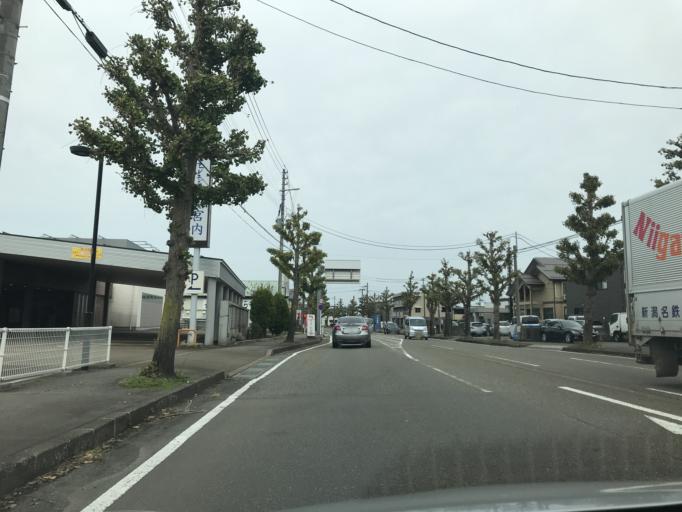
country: JP
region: Niigata
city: Nagaoka
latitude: 37.4276
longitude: 138.8360
